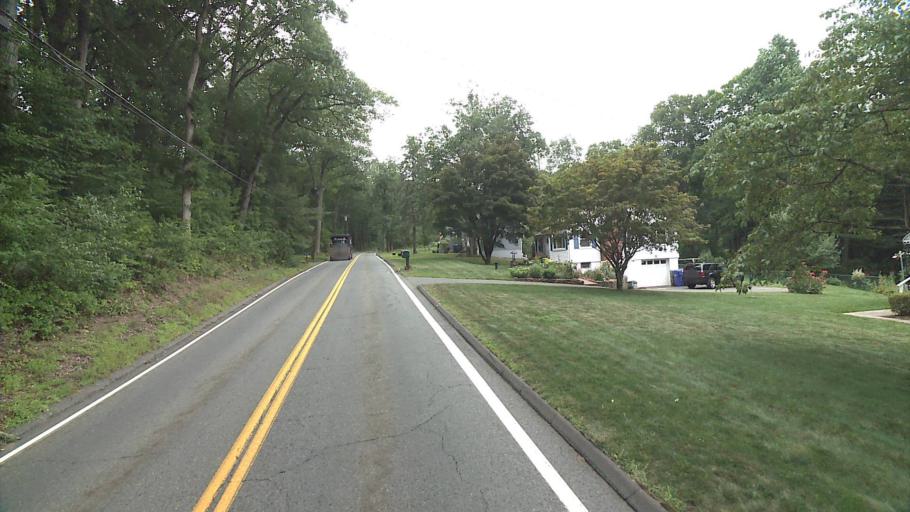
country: US
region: Connecticut
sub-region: Hartford County
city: Manchester
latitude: 41.7891
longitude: -72.4697
